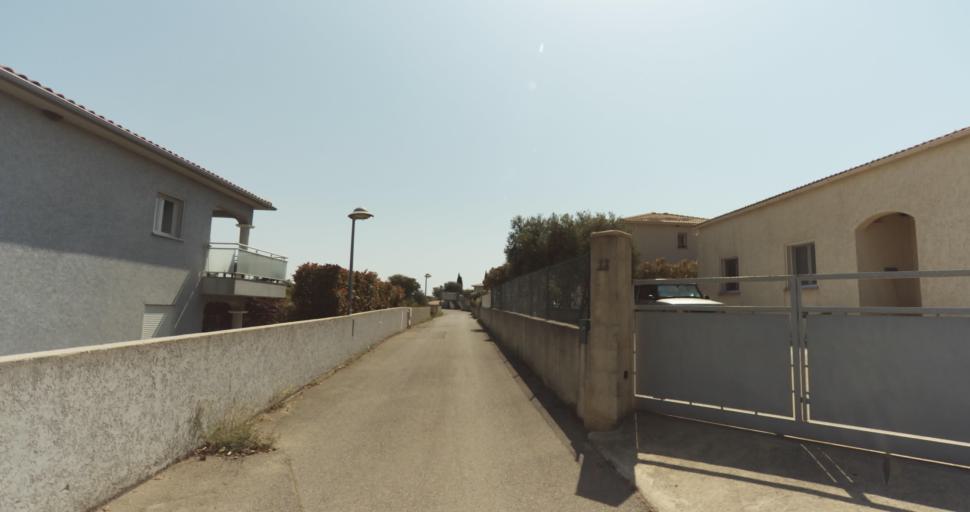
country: FR
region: Corsica
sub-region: Departement de la Haute-Corse
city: Biguglia
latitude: 42.6133
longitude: 9.4306
